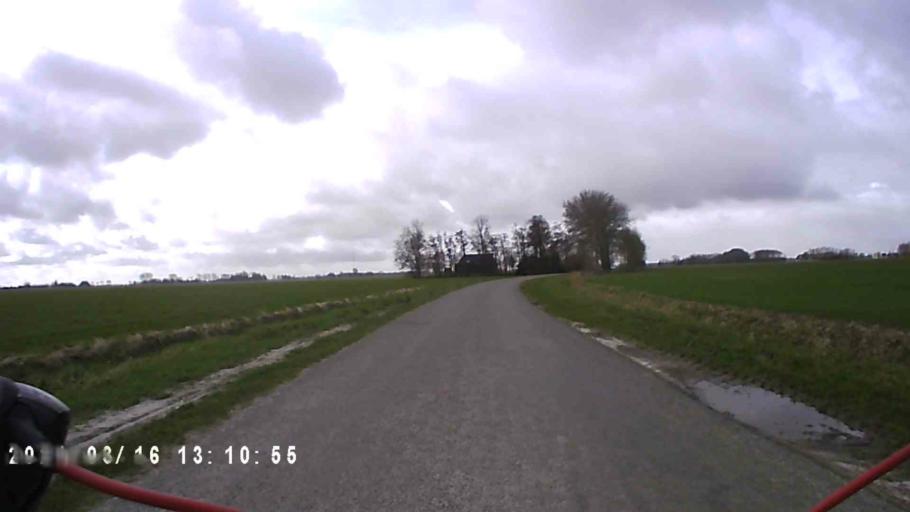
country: NL
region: Friesland
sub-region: Gemeente Het Bildt
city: Minnertsga
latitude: 53.2424
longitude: 5.6196
